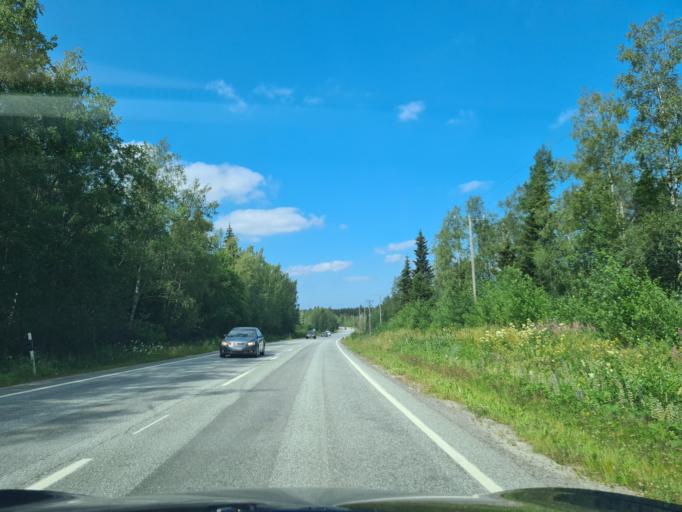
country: FI
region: Ostrobothnia
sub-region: Vaasa
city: Vaasa
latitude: 63.1852
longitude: 21.5670
